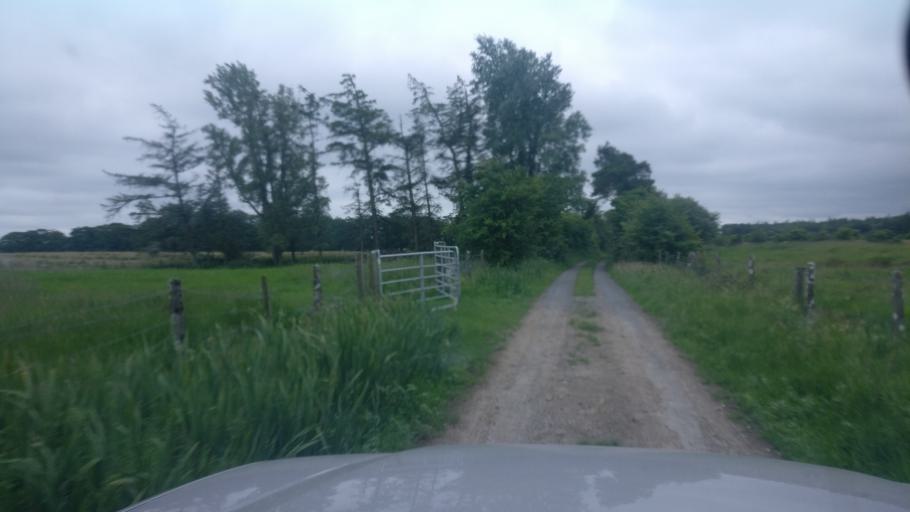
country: IE
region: Connaught
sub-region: County Galway
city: Ballinasloe
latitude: 53.2960
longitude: -8.3629
